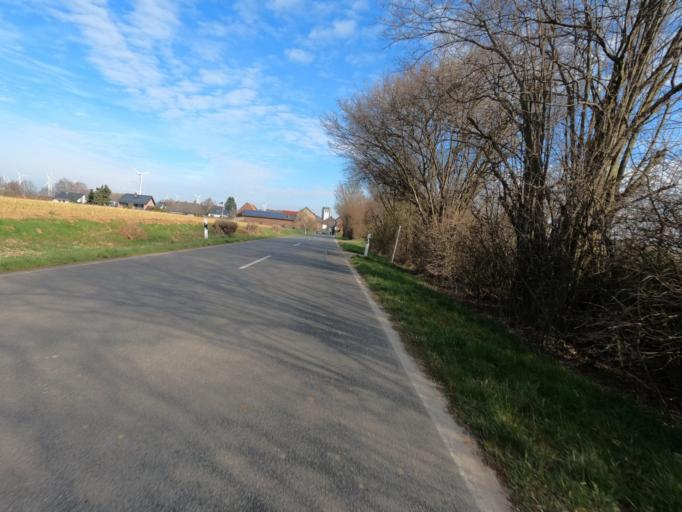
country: DE
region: North Rhine-Westphalia
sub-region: Regierungsbezirk Koln
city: Linnich
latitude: 50.9981
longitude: 6.3179
